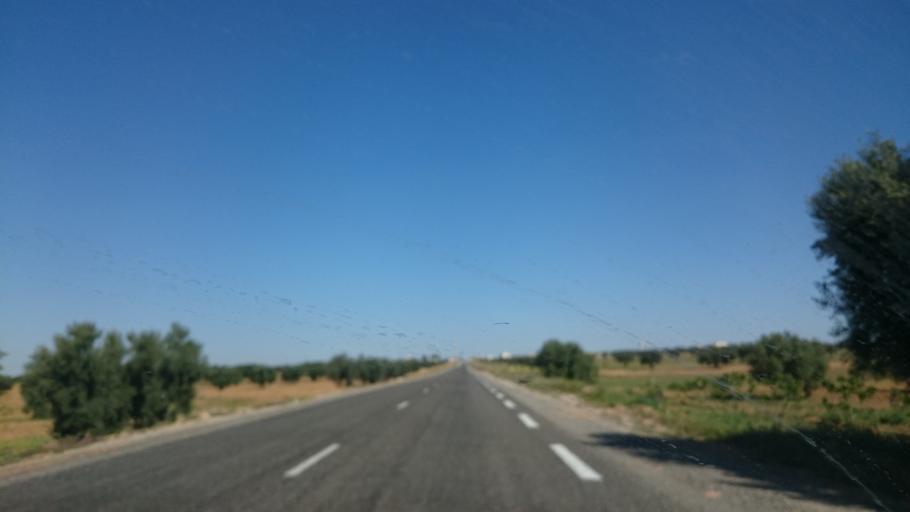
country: TN
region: Safaqis
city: Sfax
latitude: 34.8049
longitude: 10.4836
